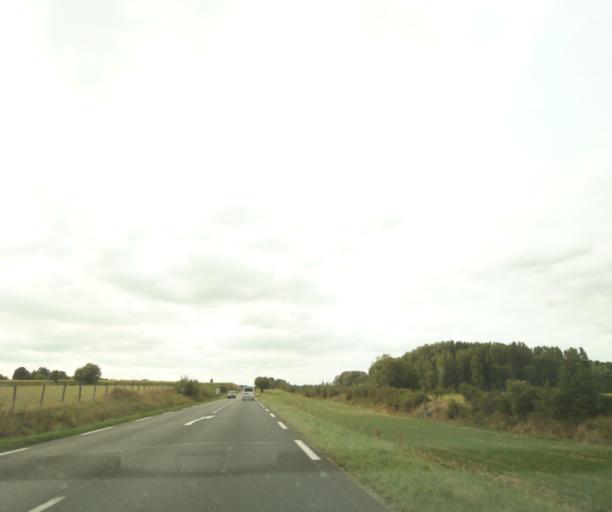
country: FR
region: Centre
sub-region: Departement d'Indre-et-Loire
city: Perrusson
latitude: 47.0793
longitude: 1.0478
